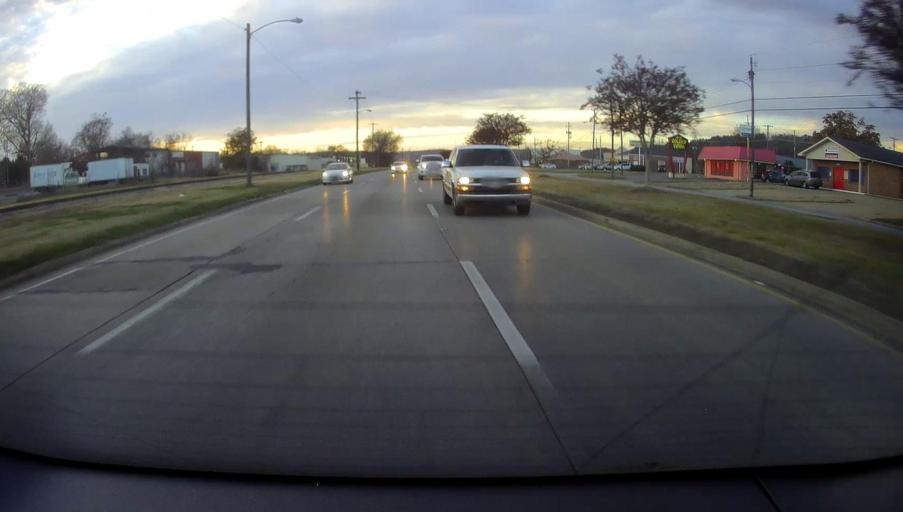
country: US
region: Alabama
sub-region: Etowah County
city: Gadsden
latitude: 34.0188
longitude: -86.0144
